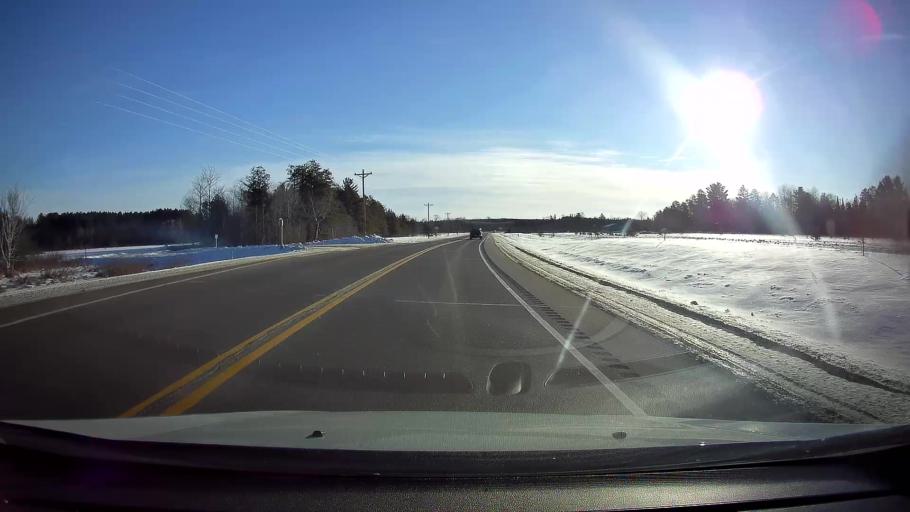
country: US
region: Wisconsin
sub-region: Sawyer County
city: Hayward
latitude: 45.9972
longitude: -91.6004
